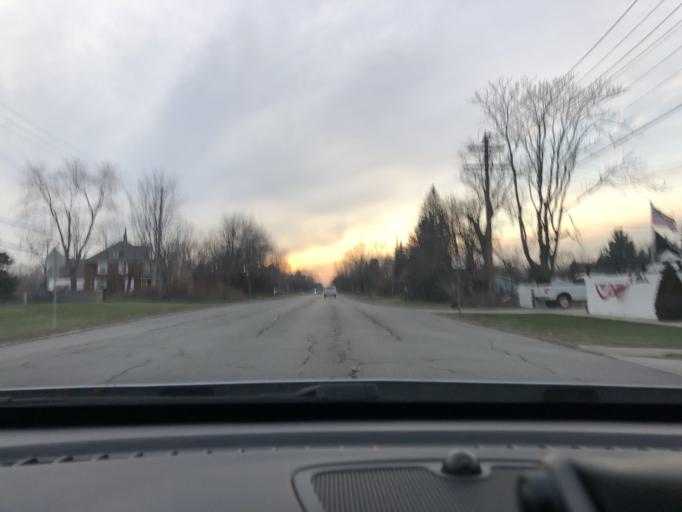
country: US
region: Michigan
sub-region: Wayne County
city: Allen Park
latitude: 42.2421
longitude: -83.2340
